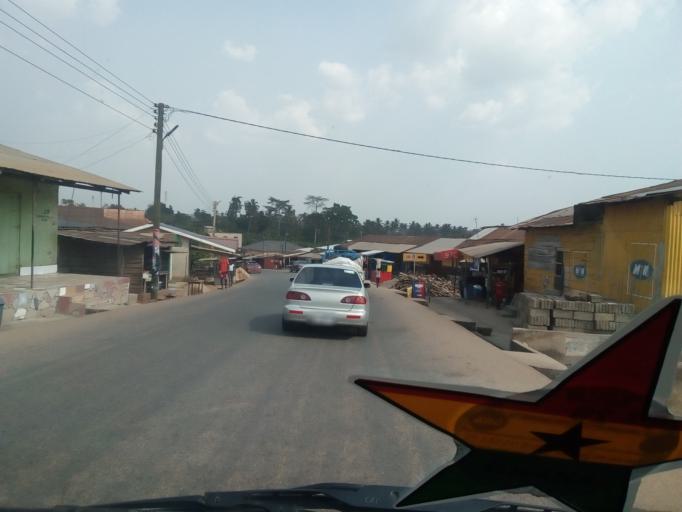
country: GH
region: Eastern
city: Suhum
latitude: 6.0412
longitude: -0.4471
